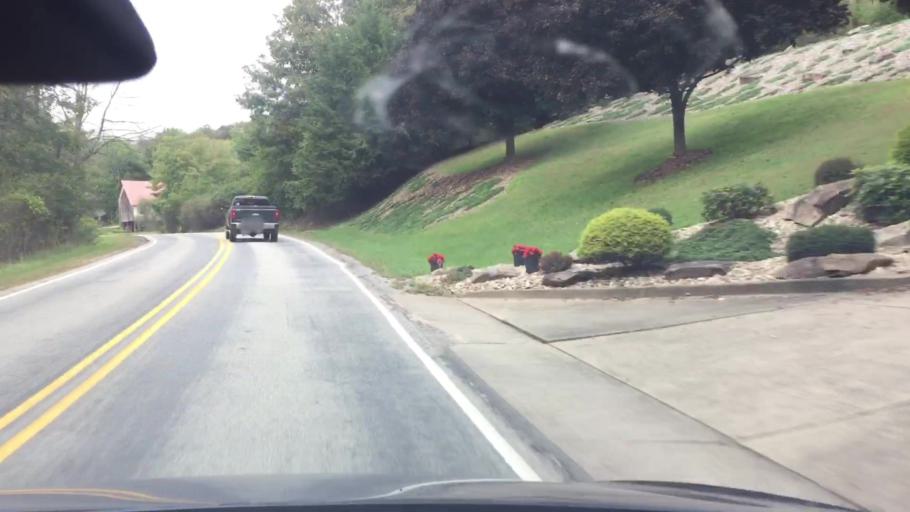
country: US
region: Pennsylvania
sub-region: Allegheny County
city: Curtisville
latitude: 40.6976
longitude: -79.8416
